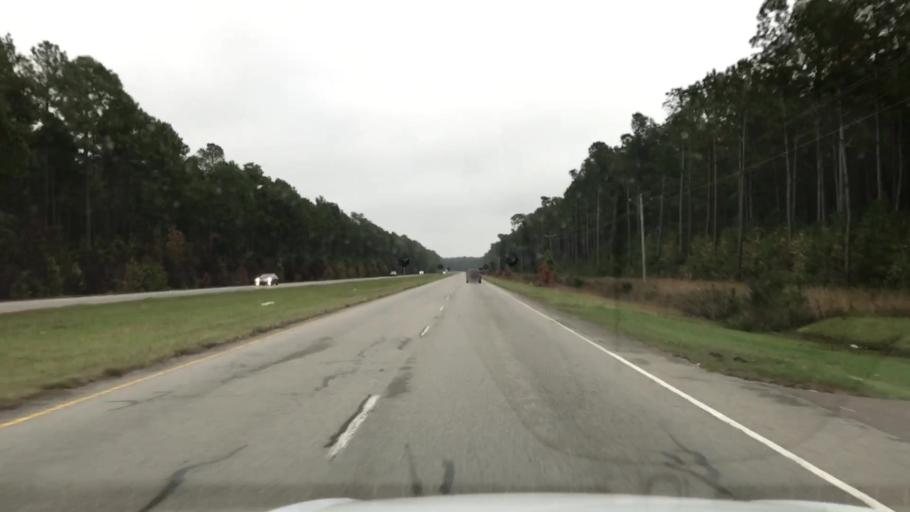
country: US
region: South Carolina
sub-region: Charleston County
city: Awendaw
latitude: 33.0453
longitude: -79.5793
